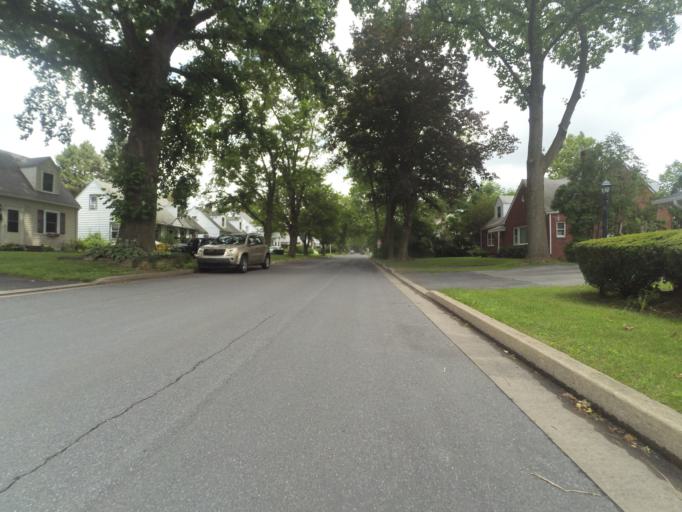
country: US
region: Pennsylvania
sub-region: Centre County
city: State College
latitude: 40.7840
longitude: -77.8725
